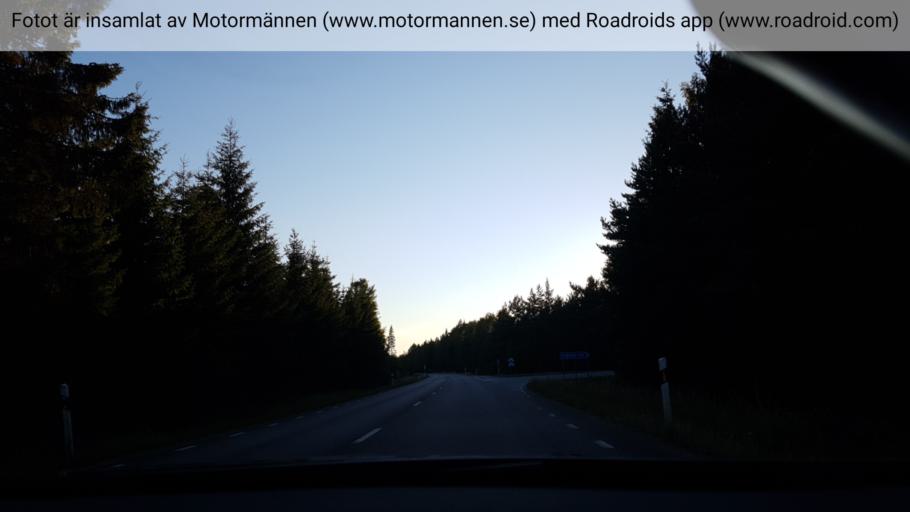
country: SE
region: Vaestra Goetaland
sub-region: Hjo Kommun
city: Hjo
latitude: 58.3397
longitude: 14.2297
